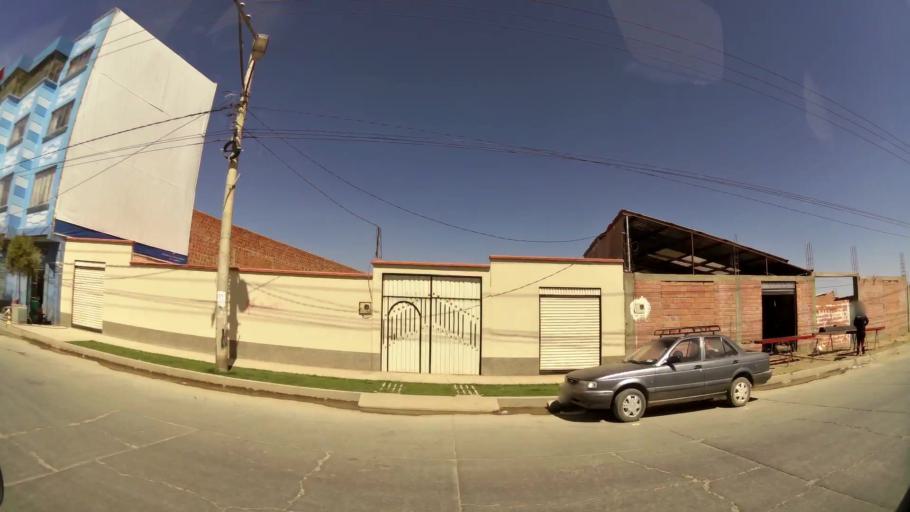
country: BO
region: La Paz
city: La Paz
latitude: -16.5475
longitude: -68.1940
